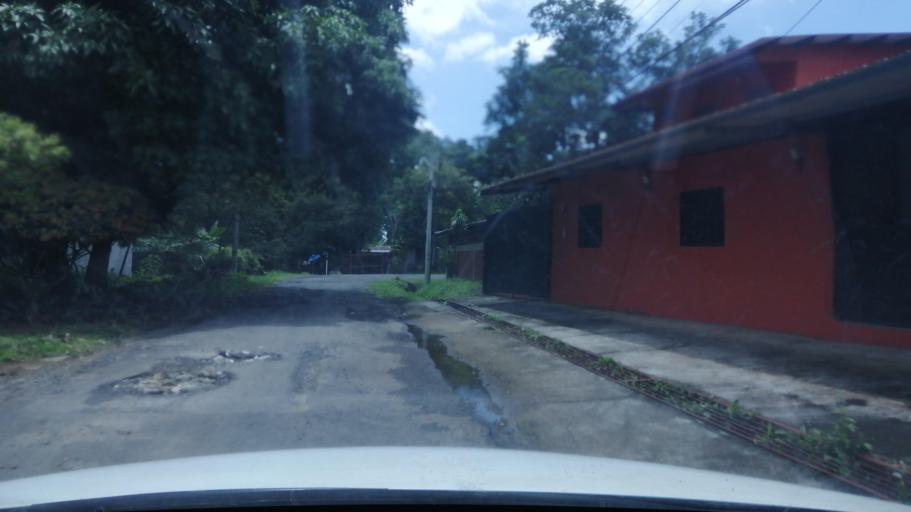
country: PA
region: Chiriqui
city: David
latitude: 8.4238
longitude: -82.4398
